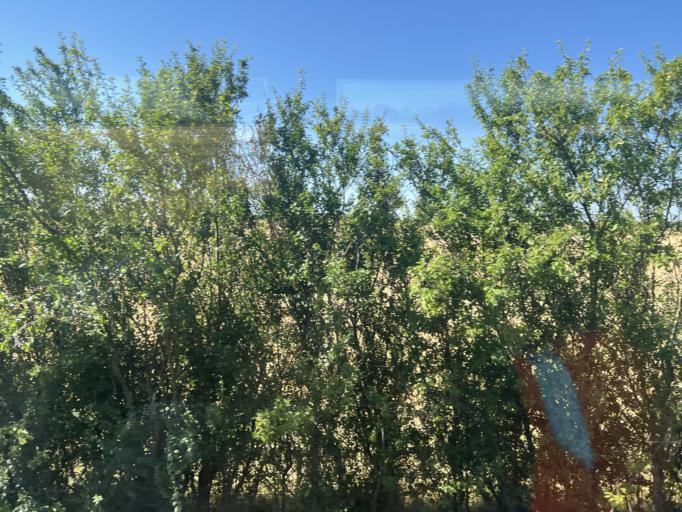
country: GB
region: England
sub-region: Lincolnshire
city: Heckington
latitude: 52.9866
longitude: -0.3424
